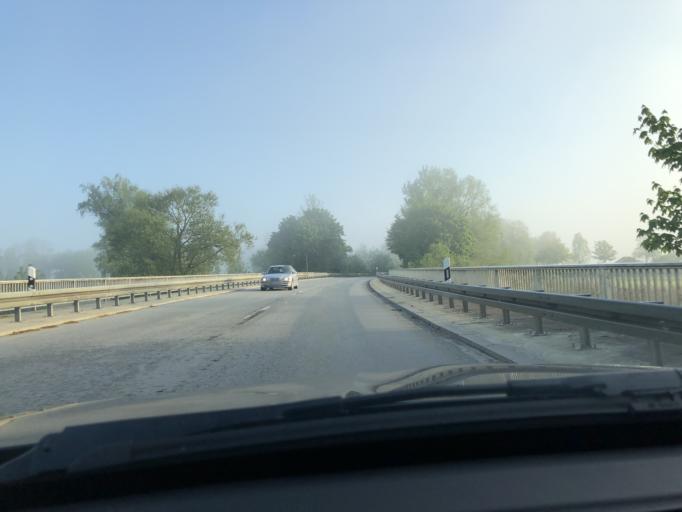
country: DE
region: Bavaria
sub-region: Upper Bavaria
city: Wolfersdorf
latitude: 48.4518
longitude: 11.7082
